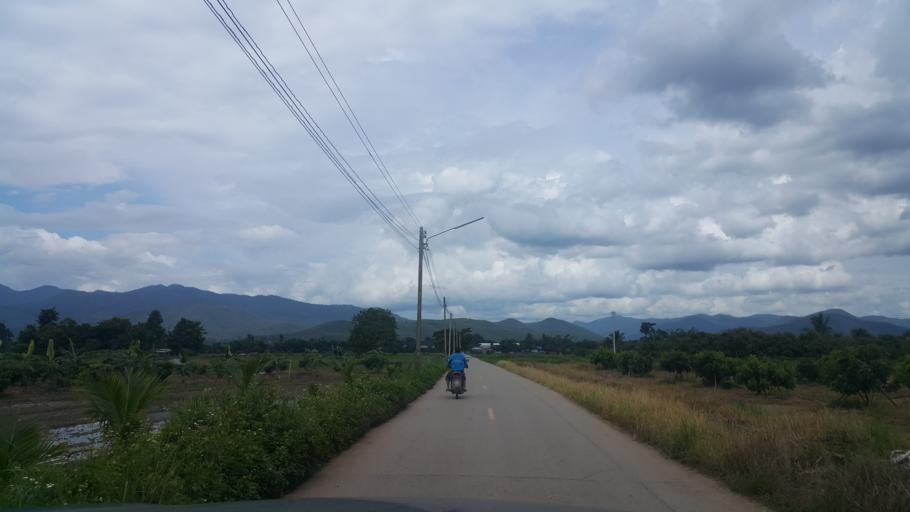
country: TH
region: Chiang Mai
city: Mae Taeng
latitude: 19.1814
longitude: 98.9827
